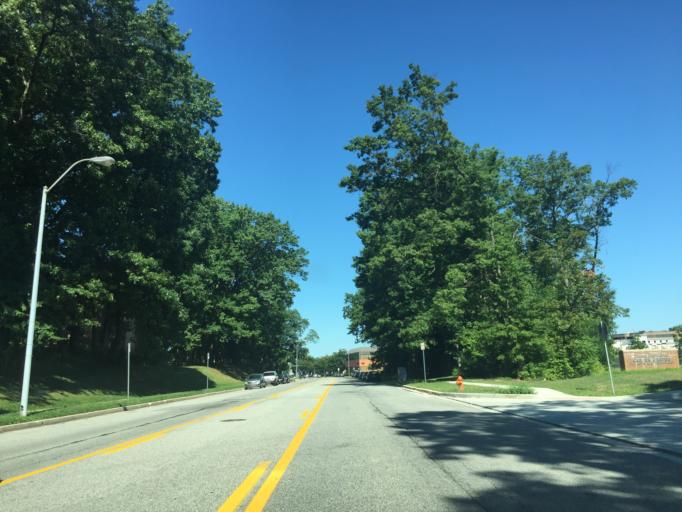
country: US
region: Maryland
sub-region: Baltimore County
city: Towson
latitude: 39.4082
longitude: -76.6121
